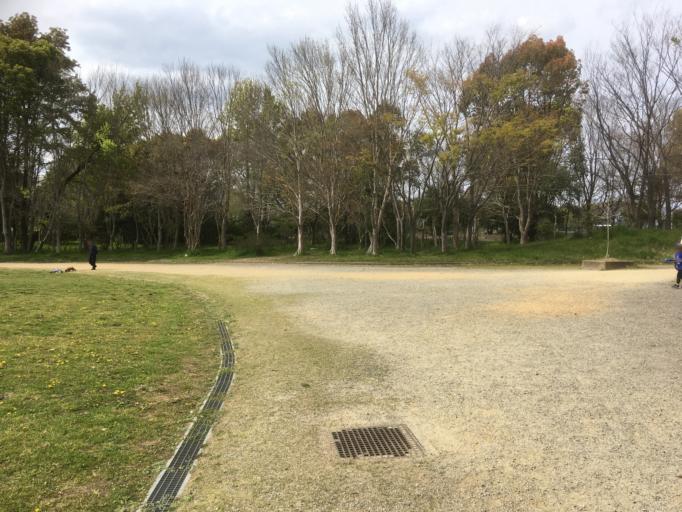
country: JP
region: Nara
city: Tawaramoto
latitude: 34.5976
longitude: 135.7826
